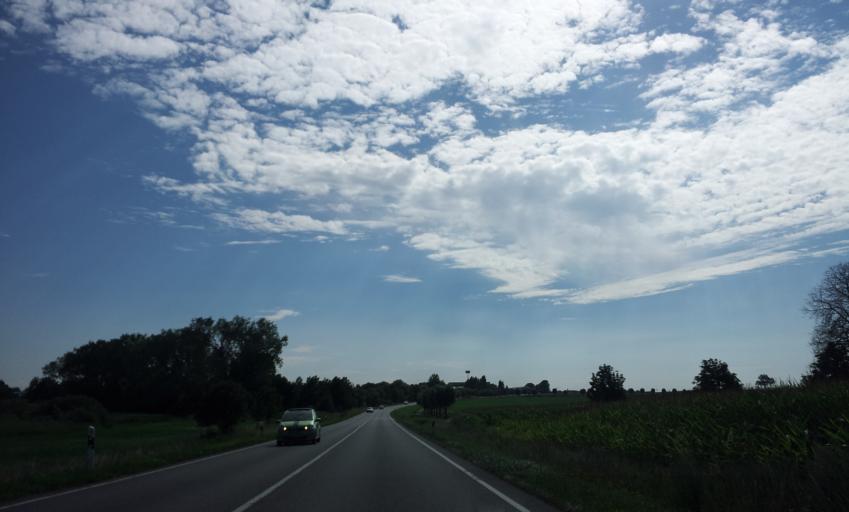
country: DE
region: Mecklenburg-Vorpommern
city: Bergen auf Ruegen
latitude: 54.4303
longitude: 13.4214
